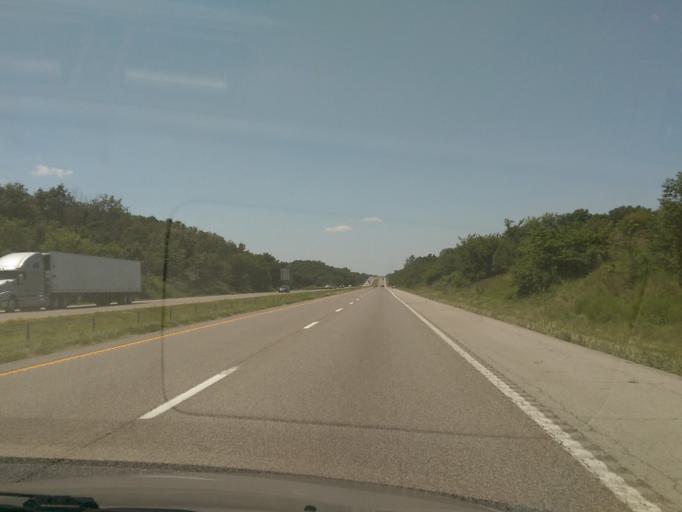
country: US
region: Missouri
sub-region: Saline County
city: Marshall
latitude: 38.9547
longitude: -93.1107
